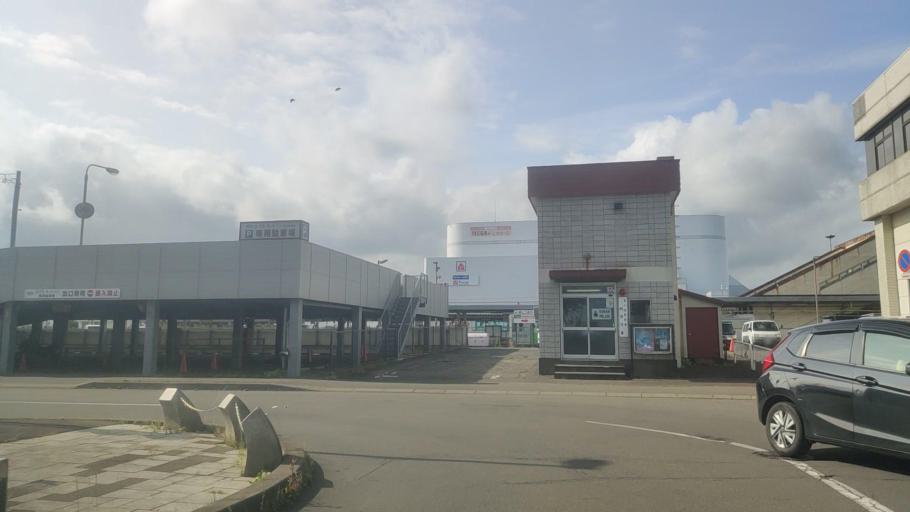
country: JP
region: Hokkaido
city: Tomakomai
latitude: 42.6390
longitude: 141.5966
